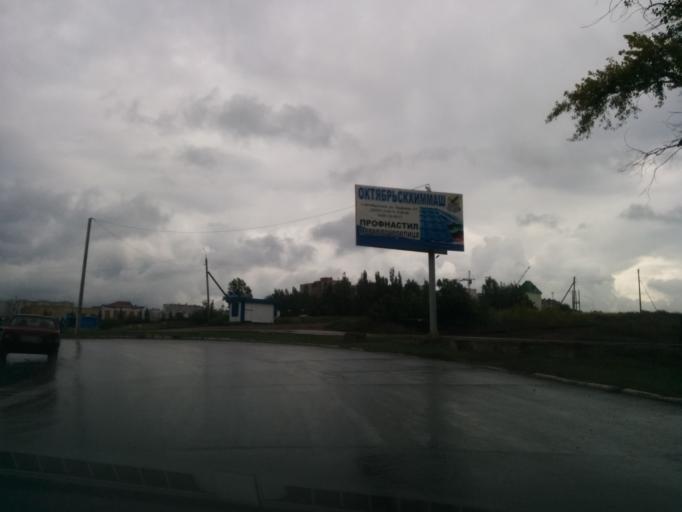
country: RU
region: Bashkortostan
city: Oktyabr'skiy
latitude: 54.4833
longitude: 53.4975
